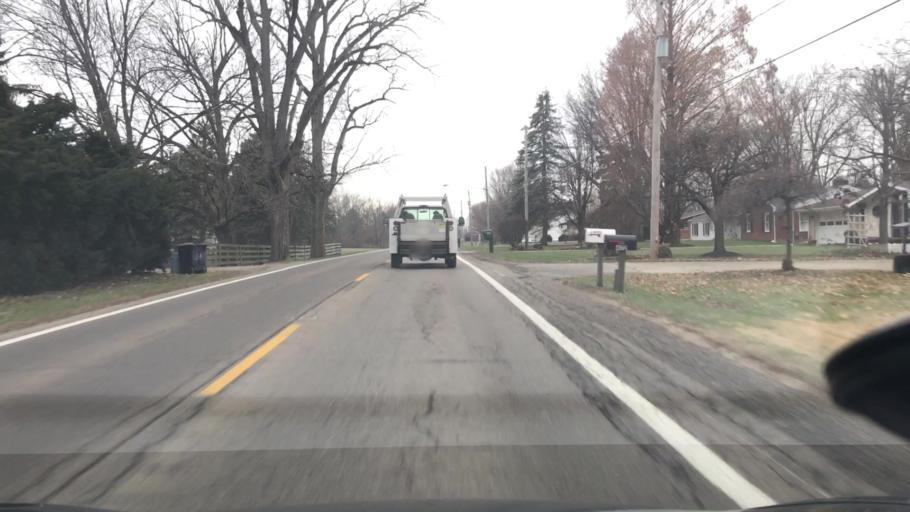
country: US
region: Ohio
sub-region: Madison County
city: London
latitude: 39.8987
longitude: -83.4635
